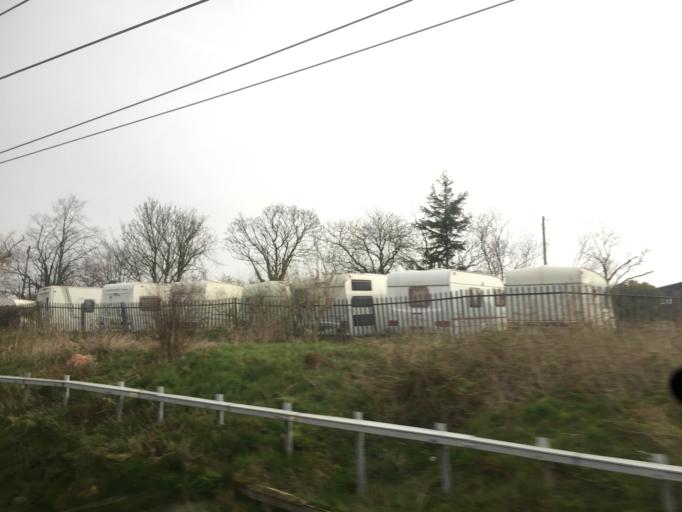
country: GB
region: England
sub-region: Lancashire
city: Coppull
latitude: 53.6129
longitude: -2.6546
